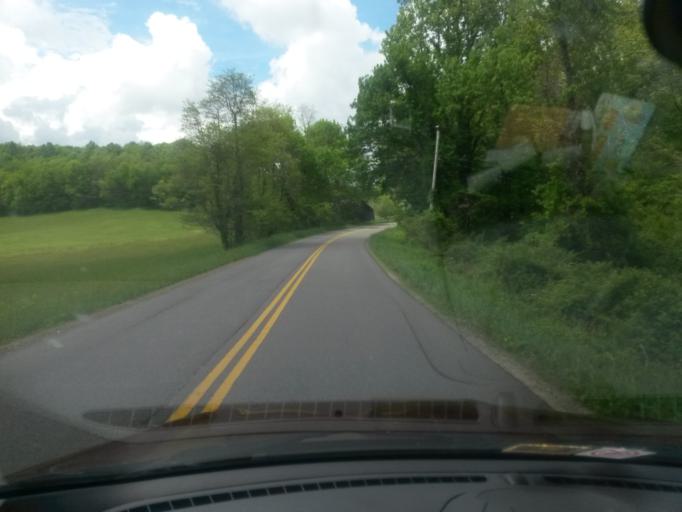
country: US
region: Virginia
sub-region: Floyd County
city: Floyd
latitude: 36.7757
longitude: -80.3912
